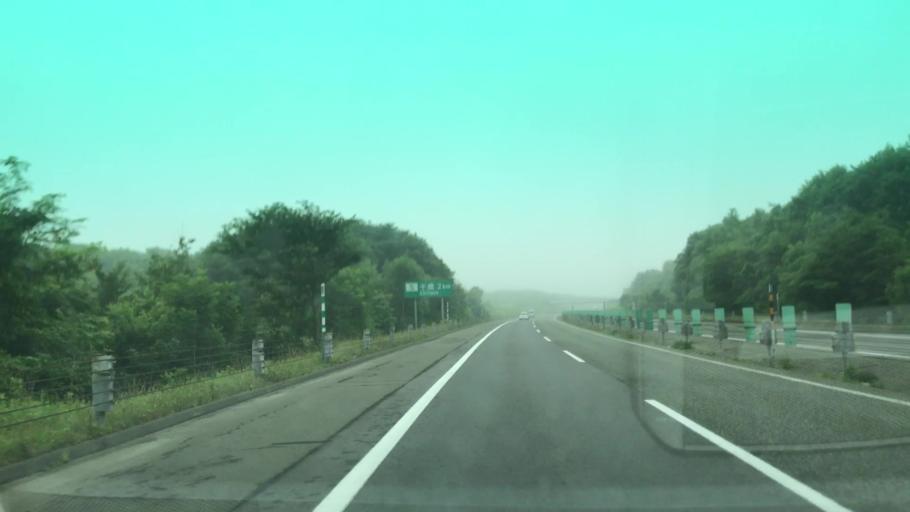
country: JP
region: Hokkaido
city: Chitose
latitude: 42.8305
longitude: 141.6121
